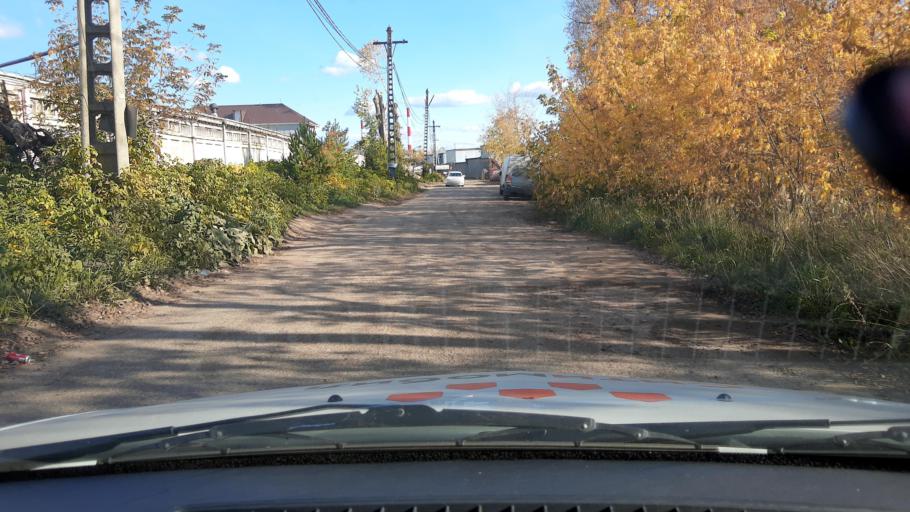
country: RU
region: Bashkortostan
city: Ufa
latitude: 54.7959
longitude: 56.0906
